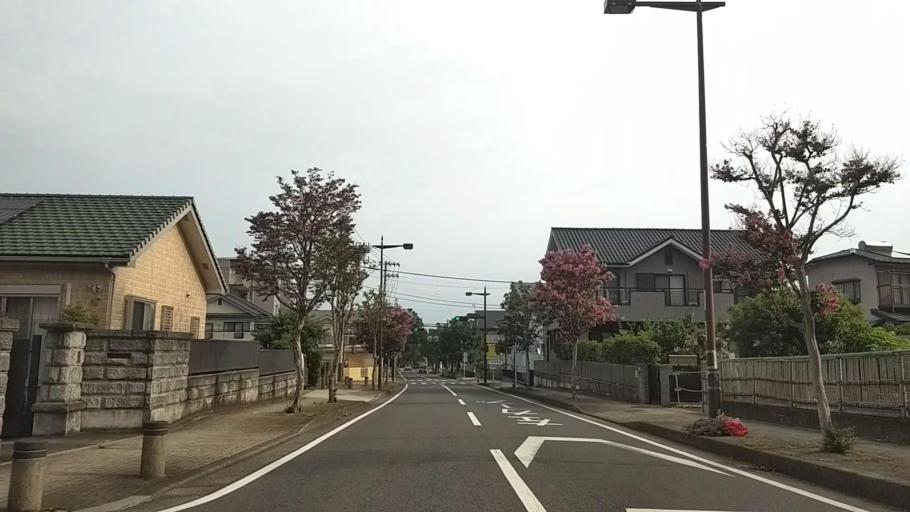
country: JP
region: Kanagawa
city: Oiso
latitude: 35.3295
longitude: 139.3097
